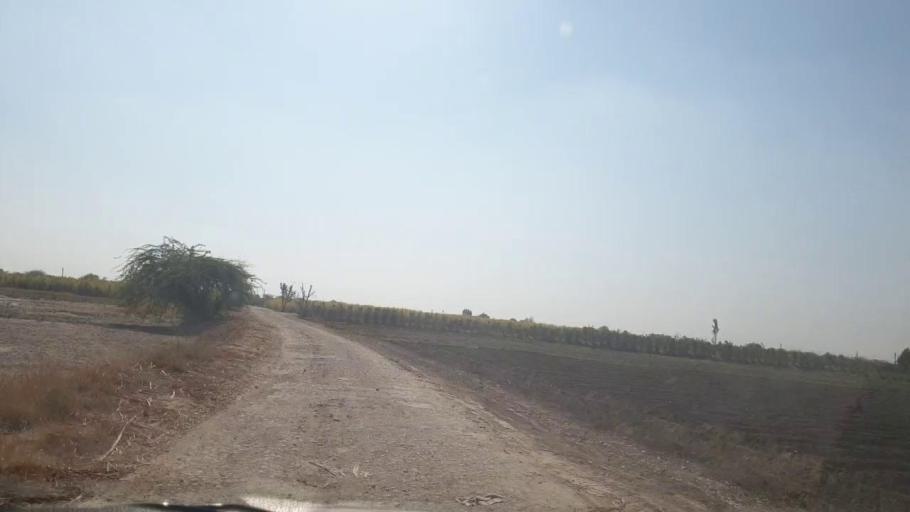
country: PK
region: Sindh
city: Mirpur Khas
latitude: 25.4749
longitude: 69.1272
